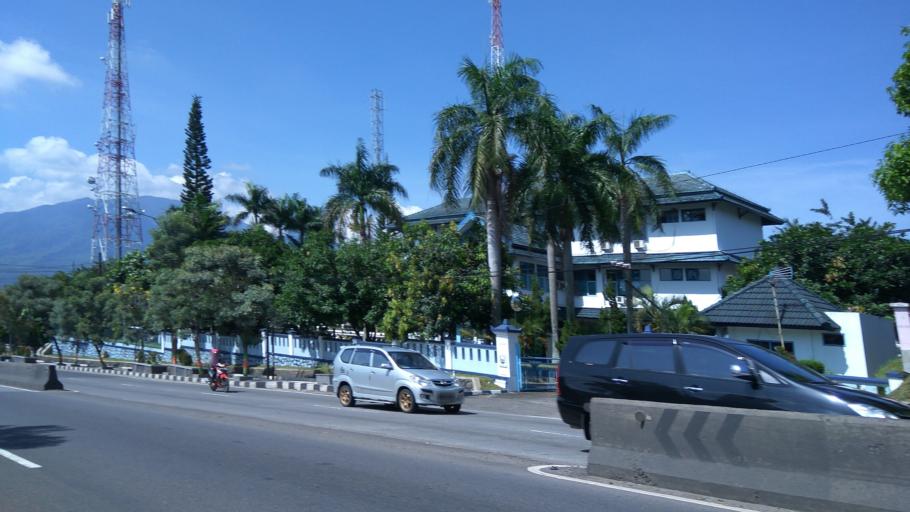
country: ID
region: Central Java
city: Ungaran
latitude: -7.1108
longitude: 110.4127
